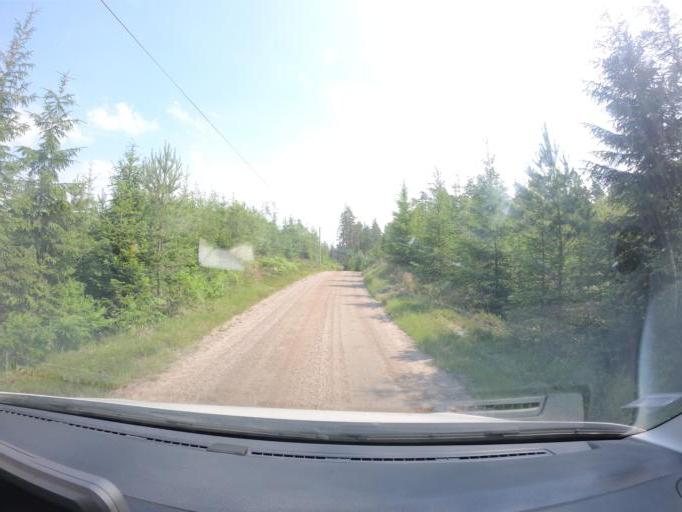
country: SE
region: Kronoberg
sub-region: Markaryds Kommun
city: Markaryd
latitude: 56.3807
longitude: 13.5545
